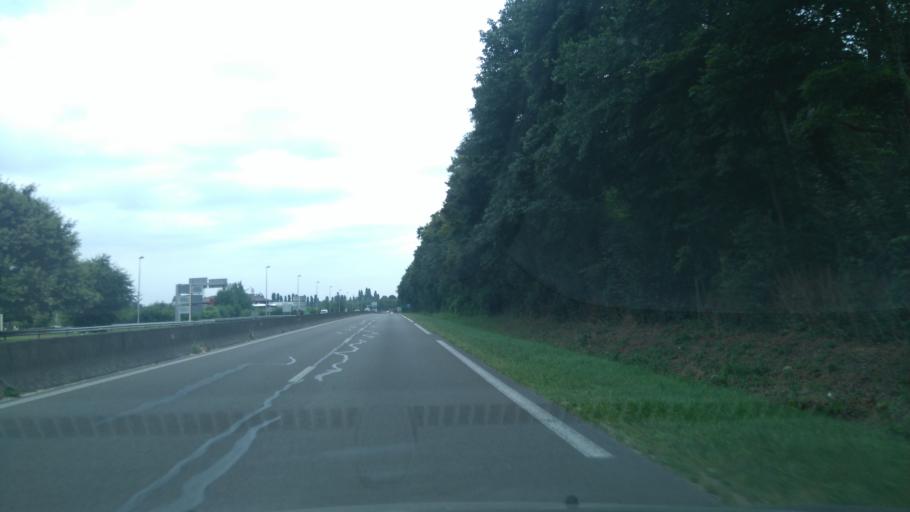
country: FR
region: Picardie
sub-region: Departement de l'Oise
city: Creil
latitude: 49.2386
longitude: 2.4730
